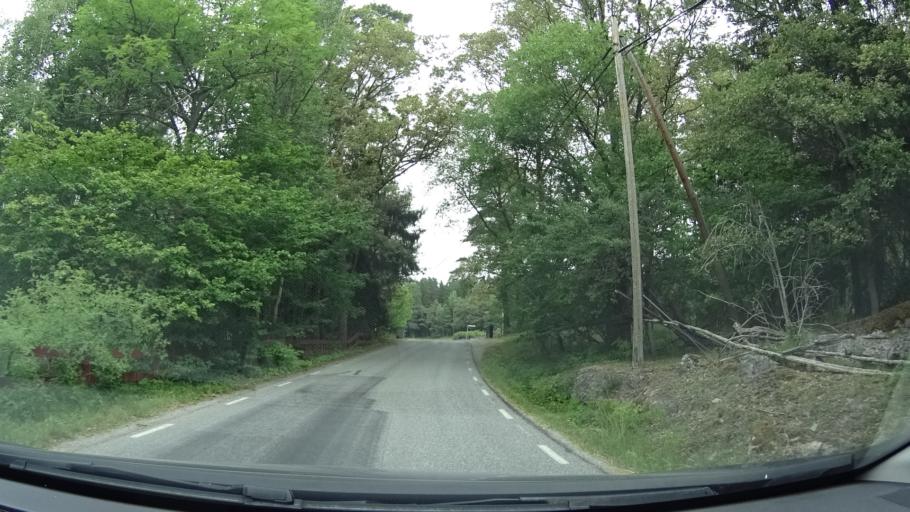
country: SE
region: Stockholm
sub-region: Varmdo Kommun
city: Mortnas
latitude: 59.3738
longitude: 18.4652
